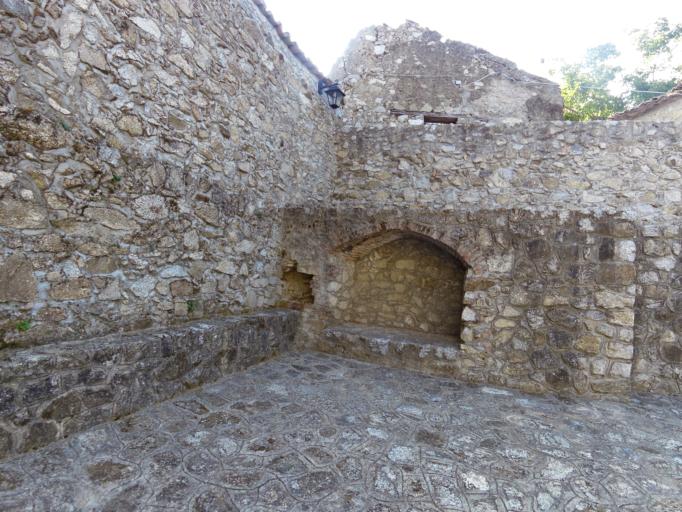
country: IT
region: Calabria
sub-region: Provincia di Vibo-Valentia
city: Nardodipace
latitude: 38.4461
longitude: 16.3472
